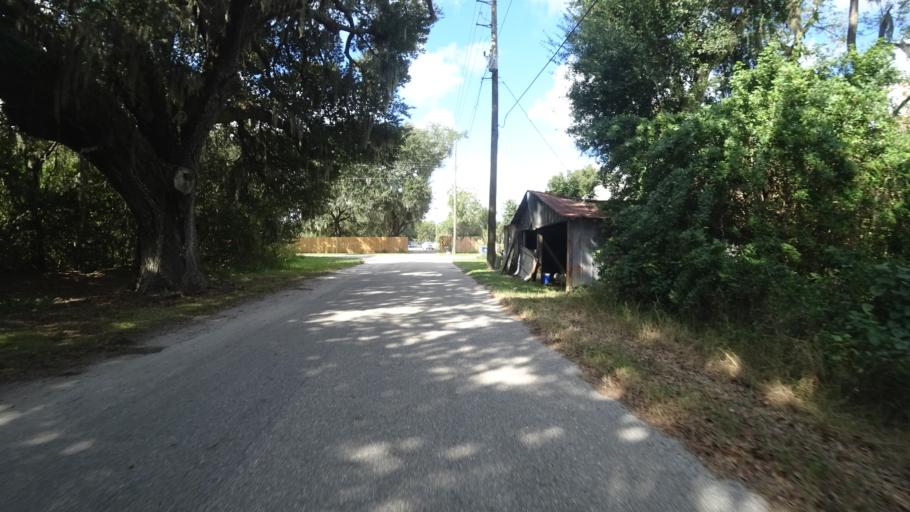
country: US
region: Florida
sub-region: Manatee County
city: Samoset
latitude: 27.4725
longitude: -82.4583
